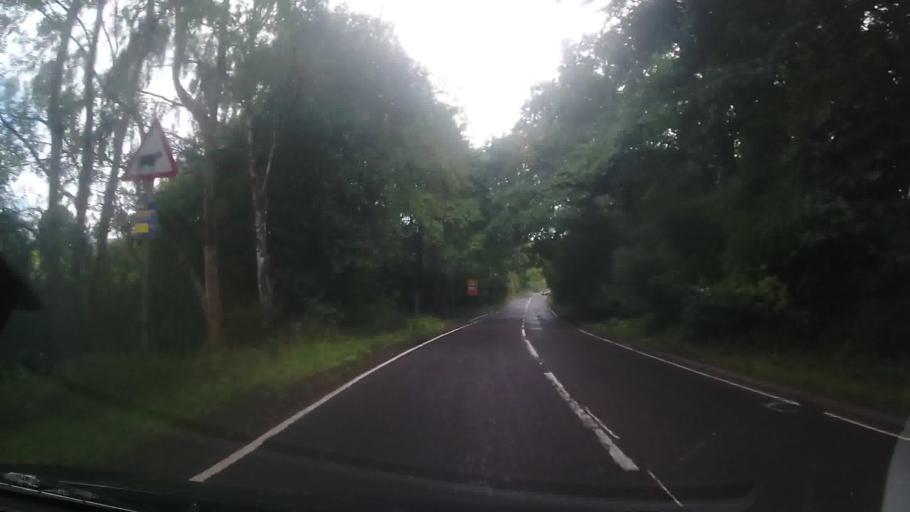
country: GB
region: England
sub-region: Shropshire
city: Much Wenlock
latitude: 52.6282
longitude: -2.5367
